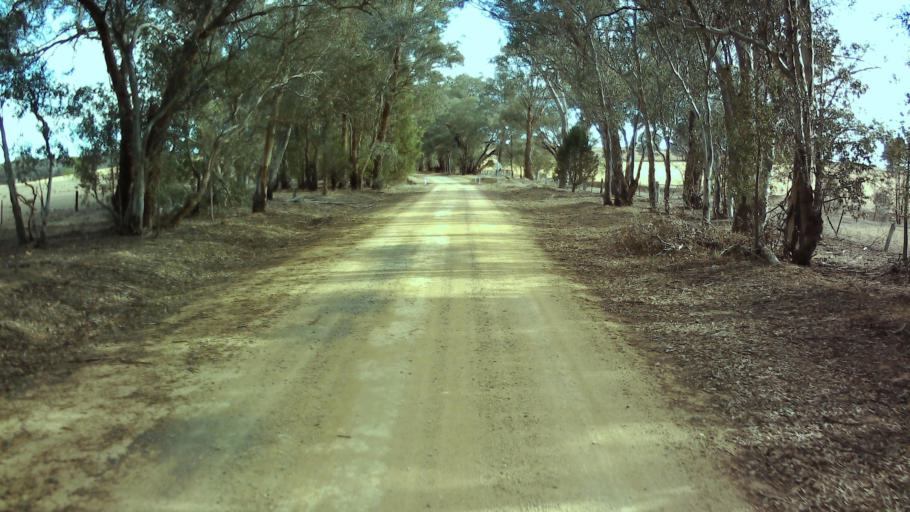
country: AU
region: New South Wales
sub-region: Weddin
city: Grenfell
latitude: -33.9007
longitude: 148.2031
